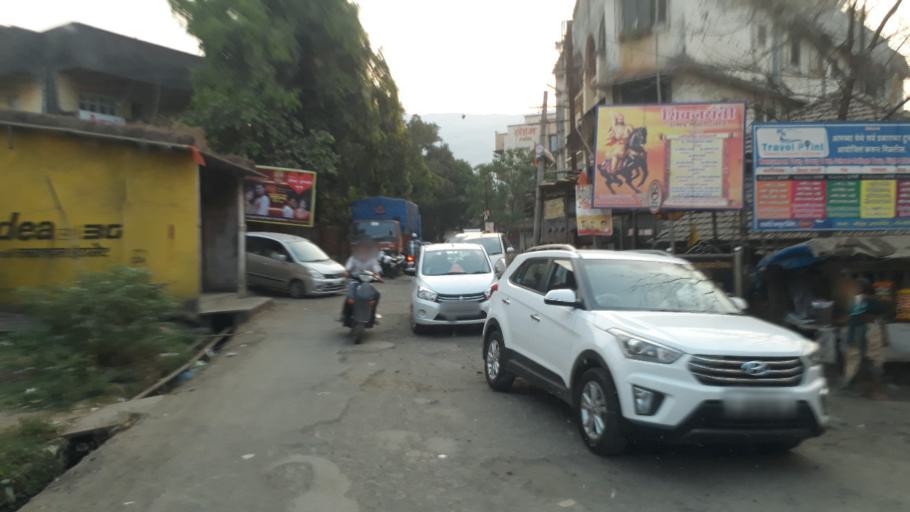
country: IN
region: Maharashtra
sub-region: Raigarh
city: Neral
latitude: 19.0233
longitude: 73.3162
